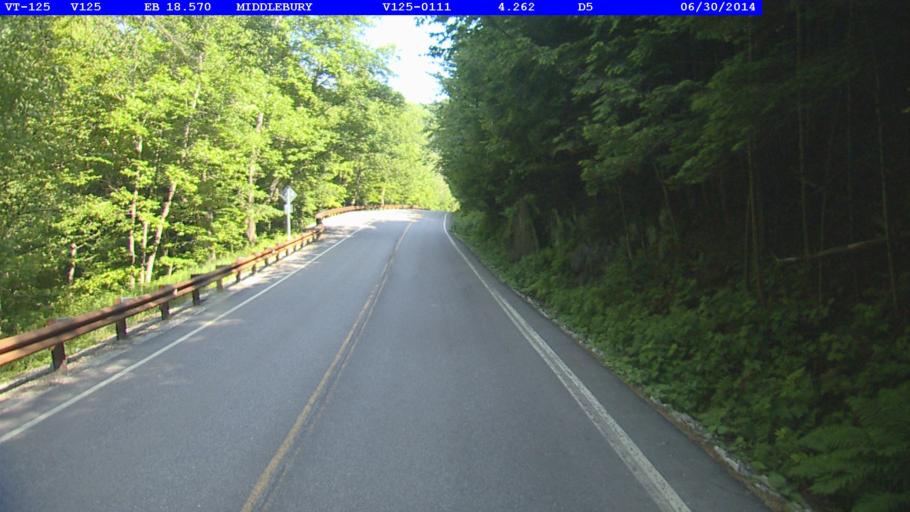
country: US
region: Vermont
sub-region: Addison County
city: Middlebury (village)
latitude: 43.9729
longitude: -73.0599
